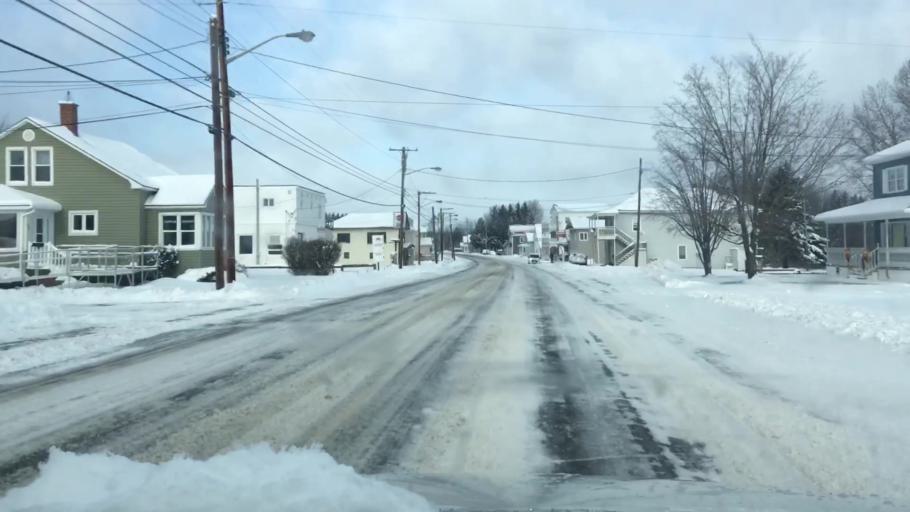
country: US
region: Maine
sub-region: Aroostook County
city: Van Buren
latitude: 47.1853
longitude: -67.9558
